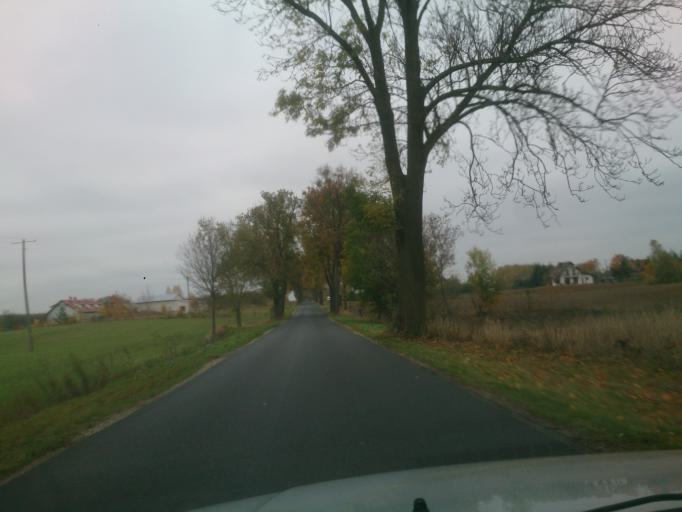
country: PL
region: Kujawsko-Pomorskie
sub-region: Powiat brodnicki
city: Brodnica
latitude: 53.3052
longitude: 19.3957
